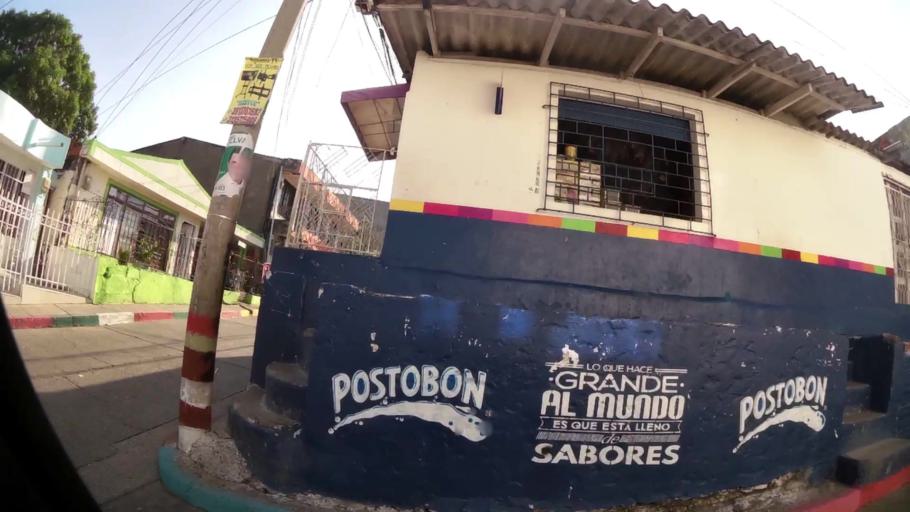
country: CO
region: Bolivar
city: Cartagena
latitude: 10.4032
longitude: -75.4821
